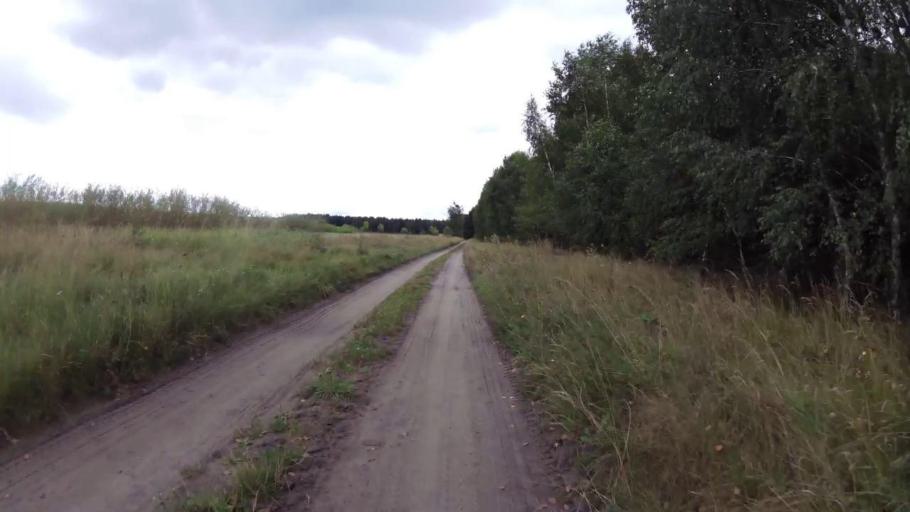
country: PL
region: West Pomeranian Voivodeship
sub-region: Powiat mysliborski
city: Debno
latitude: 52.7797
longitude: 14.7108
